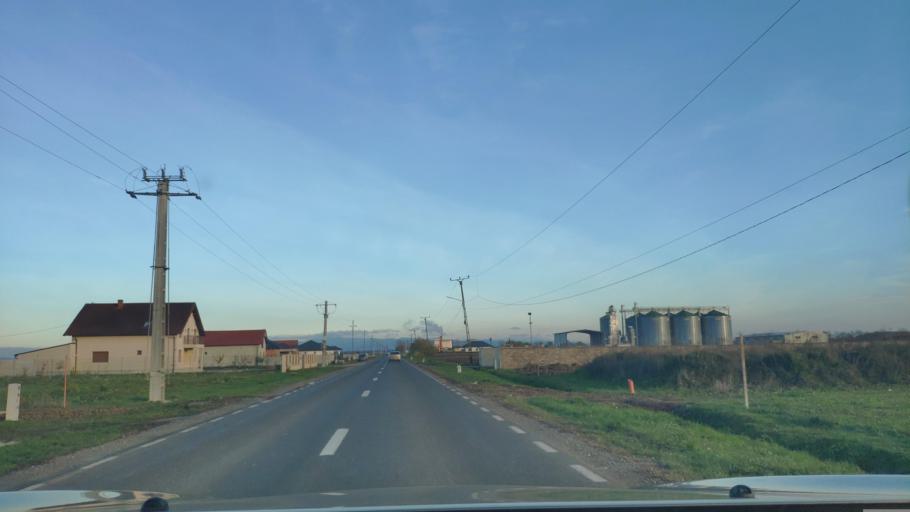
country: RO
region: Satu Mare
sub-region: Comuna Odoreu
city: Odoreu
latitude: 47.7926
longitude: 23.0116
